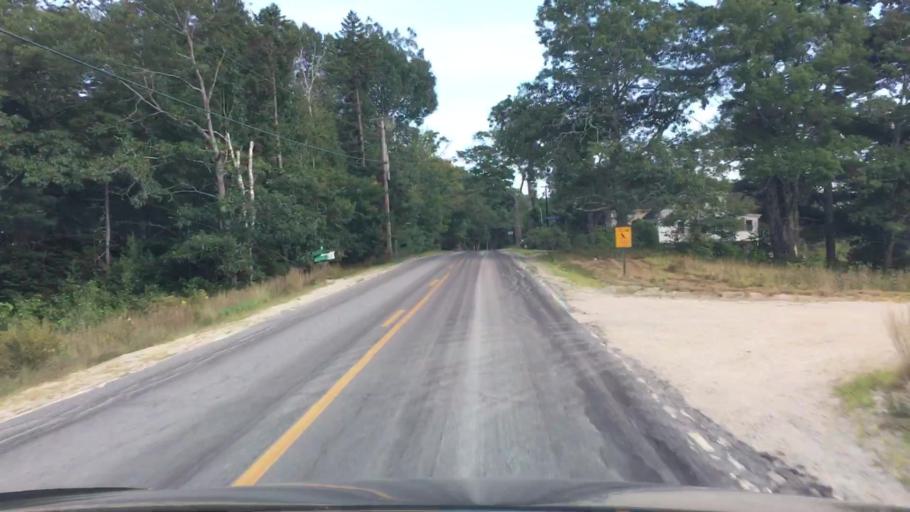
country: US
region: Maine
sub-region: Hancock County
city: Surry
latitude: 44.5130
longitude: -68.6010
